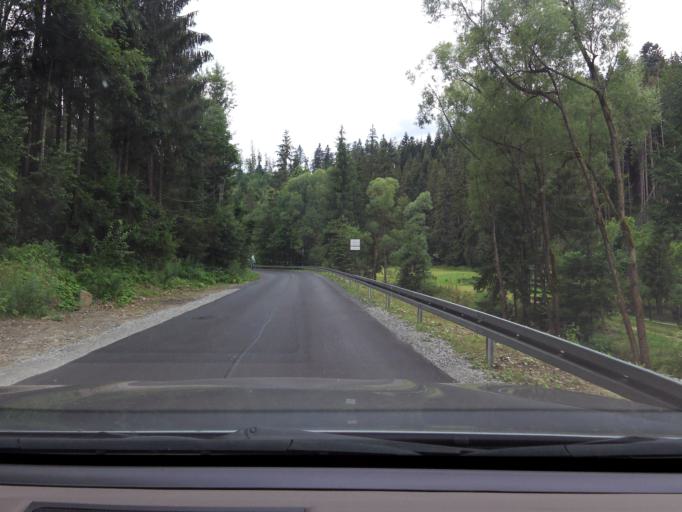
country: PL
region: Silesian Voivodeship
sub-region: Powiat zywiecki
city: Ujsoly
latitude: 49.4649
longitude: 19.1517
